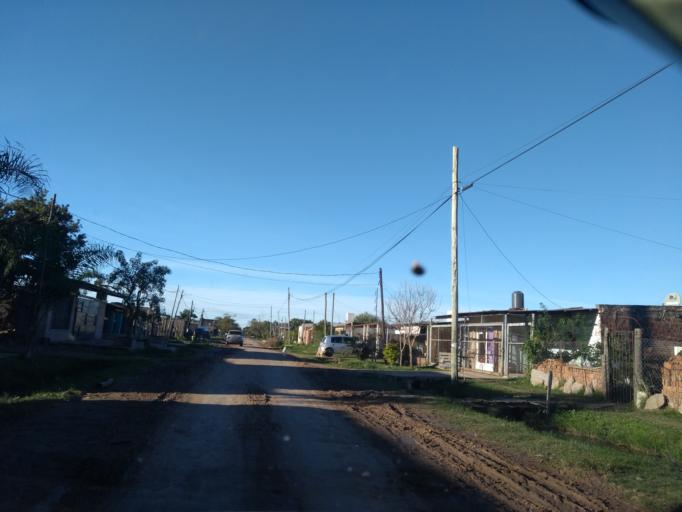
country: AR
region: Chaco
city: Barranqueras
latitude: -27.4922
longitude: -58.9378
